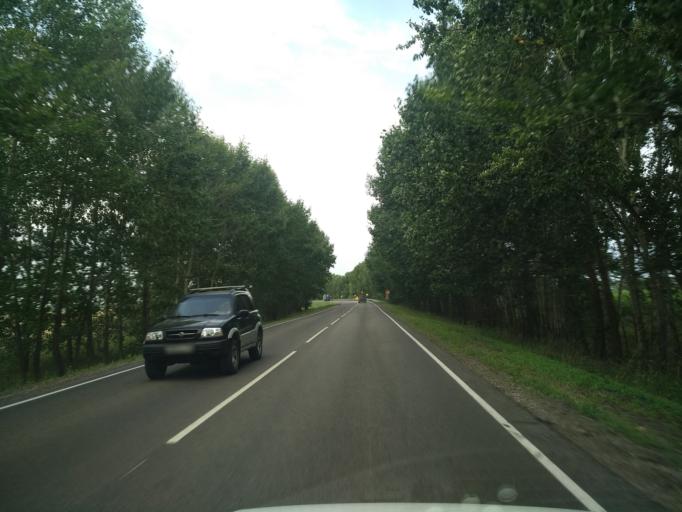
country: RU
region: Voronezj
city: Pereleshino
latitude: 51.8029
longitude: 40.1644
